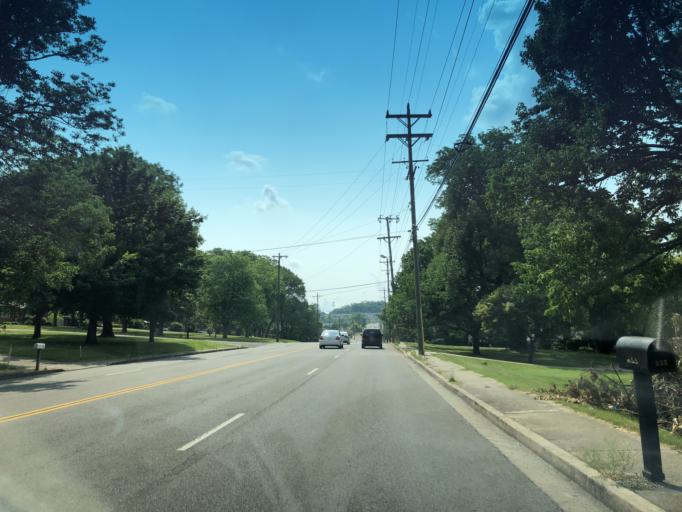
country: US
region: Tennessee
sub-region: Davidson County
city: Goodlettsville
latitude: 36.2489
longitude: -86.7314
